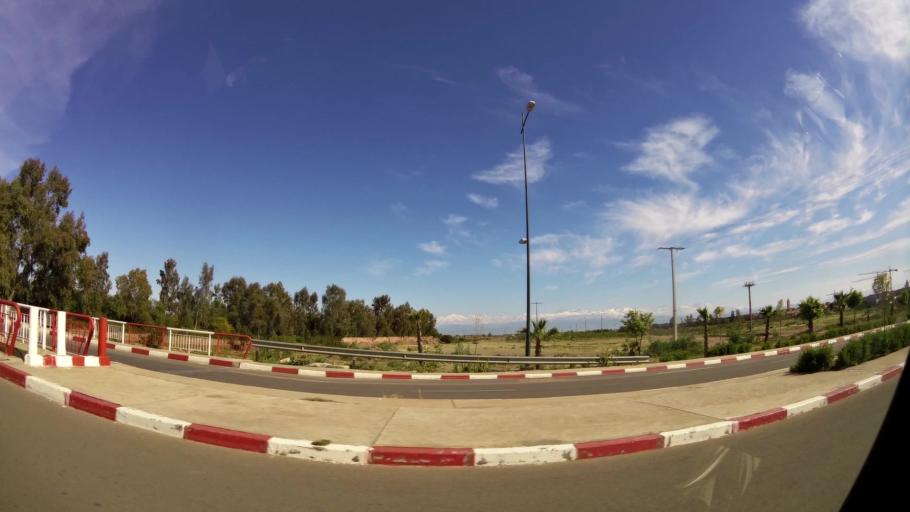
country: MA
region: Marrakech-Tensift-Al Haouz
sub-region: Marrakech
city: Marrakesh
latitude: 31.6058
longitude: -7.9564
